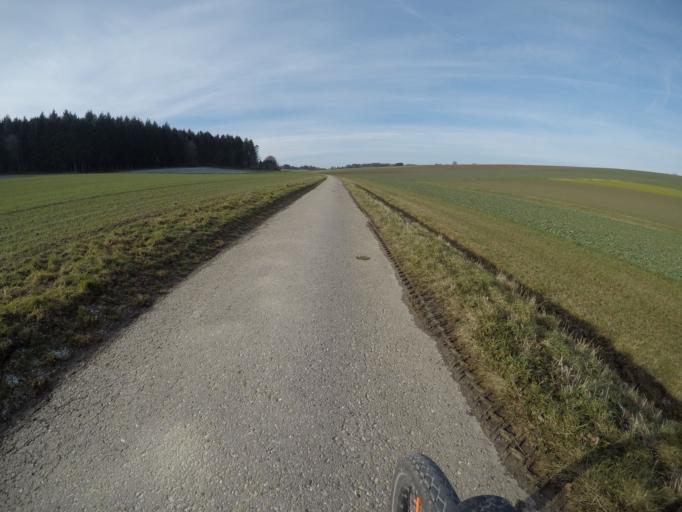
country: DE
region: Baden-Wuerttemberg
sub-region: Karlsruhe Region
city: Gechingen
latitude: 48.6950
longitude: 8.8025
